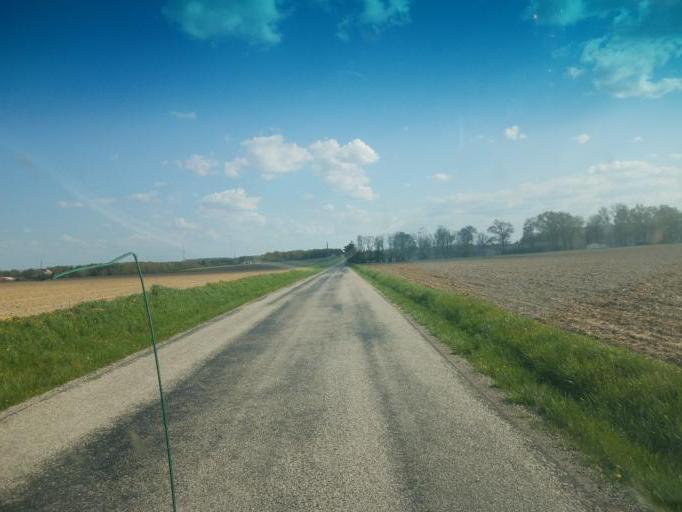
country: US
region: Ohio
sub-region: Wayne County
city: Smithville
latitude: 40.8471
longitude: -81.8779
